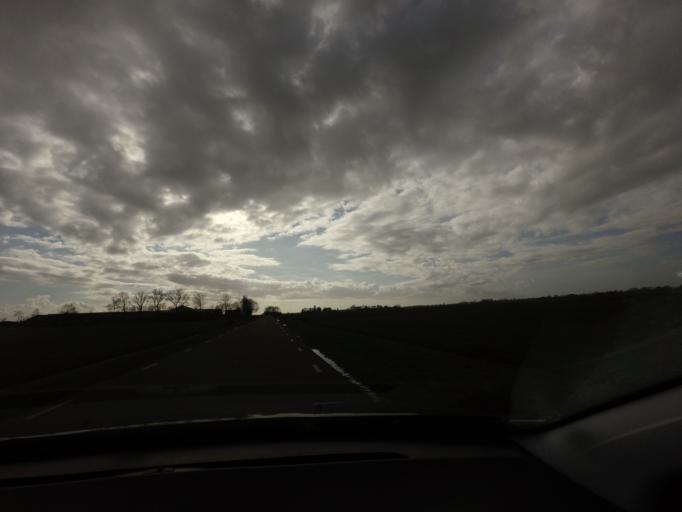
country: NL
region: Friesland
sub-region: Gemeente Boarnsterhim
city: Jirnsum
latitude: 53.0712
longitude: 5.7672
